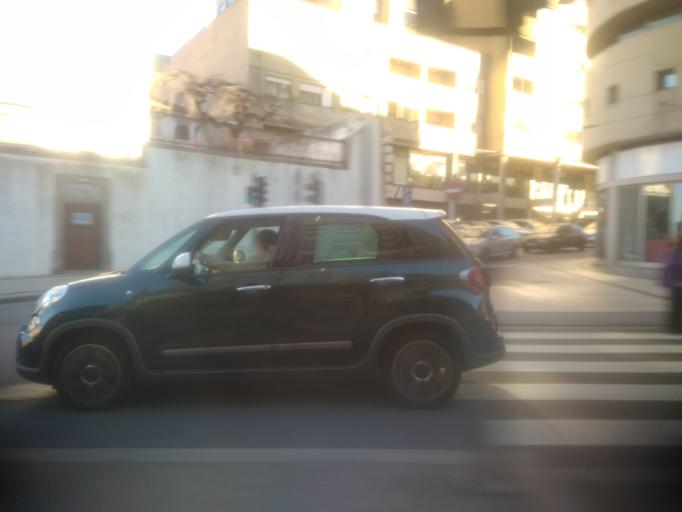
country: PT
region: Porto
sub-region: Vila Nova de Gaia
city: Vila Nova de Gaia
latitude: 41.1323
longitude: -8.6069
